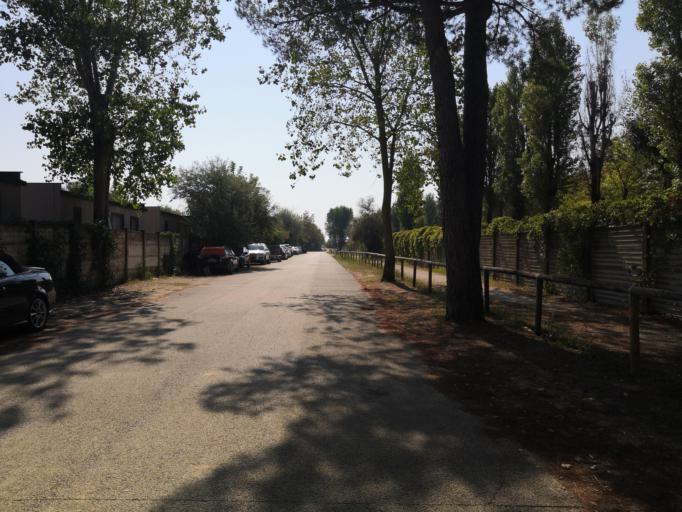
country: IT
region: Veneto
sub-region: Provincia di Venezia
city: Ca' Savio
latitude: 45.4386
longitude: 12.4443
